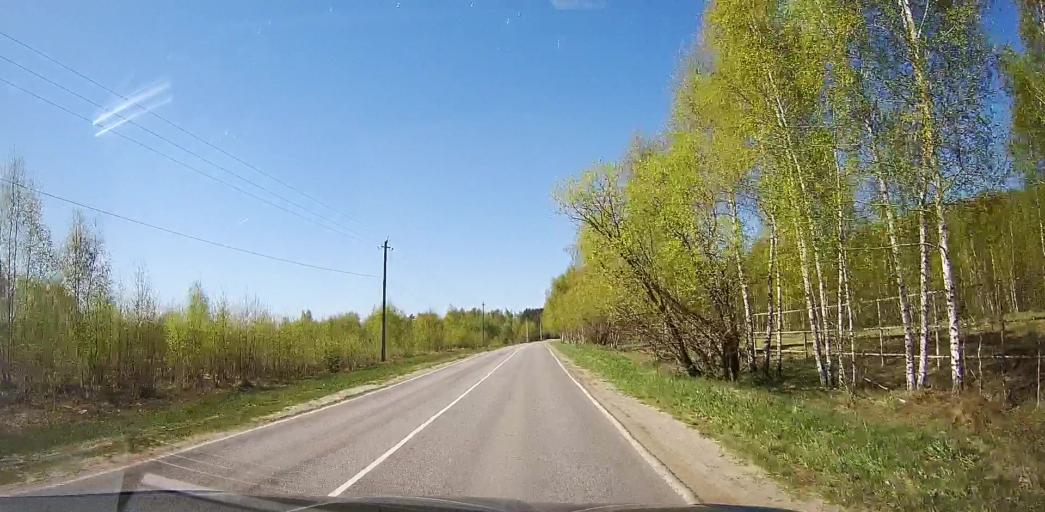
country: RU
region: Moskovskaya
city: Bronnitsy
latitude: 55.4663
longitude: 38.2809
